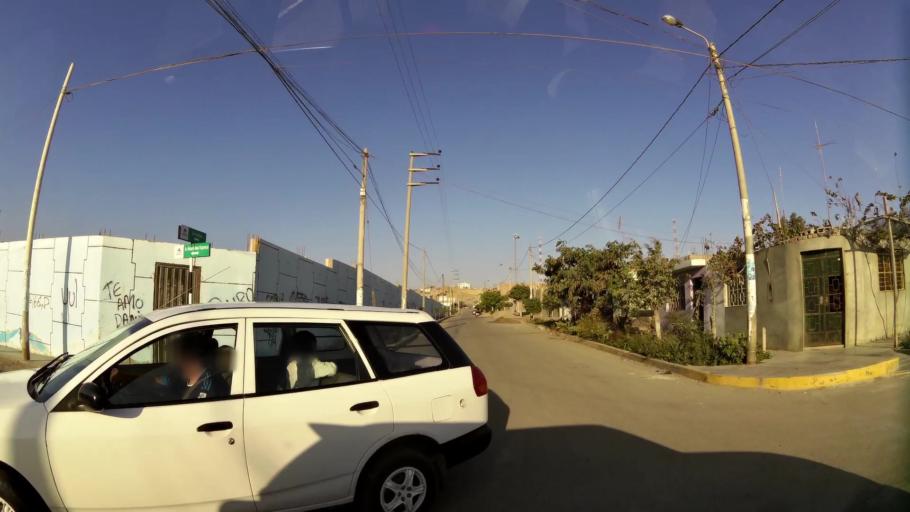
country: PE
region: Ica
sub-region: Provincia de Pisco
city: Villa Tupac Amaru
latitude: -13.7110
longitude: -76.1484
